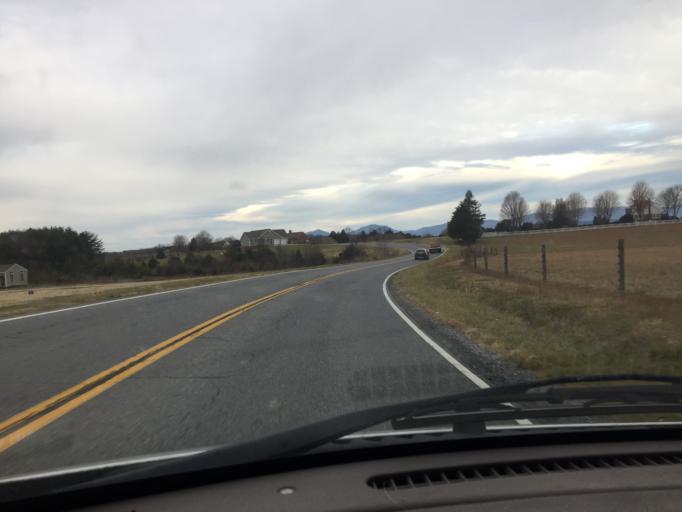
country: US
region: Virginia
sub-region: Bedford County
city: Forest
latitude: 37.3319
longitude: -79.2933
